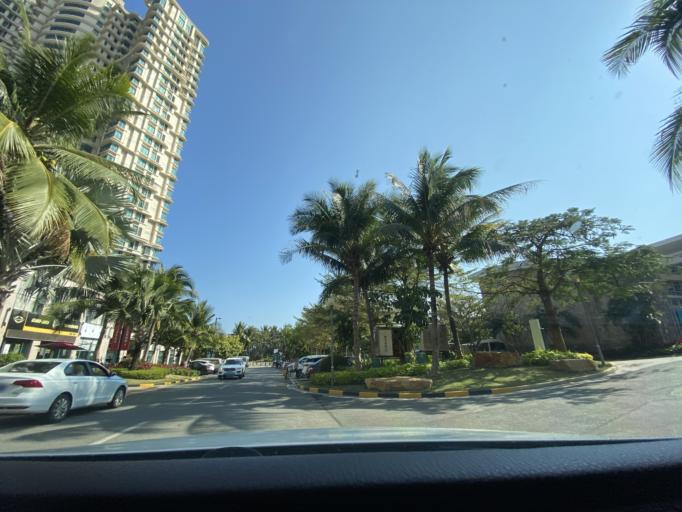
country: CN
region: Hainan
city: Yingzhou
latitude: 18.4092
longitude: 109.8751
